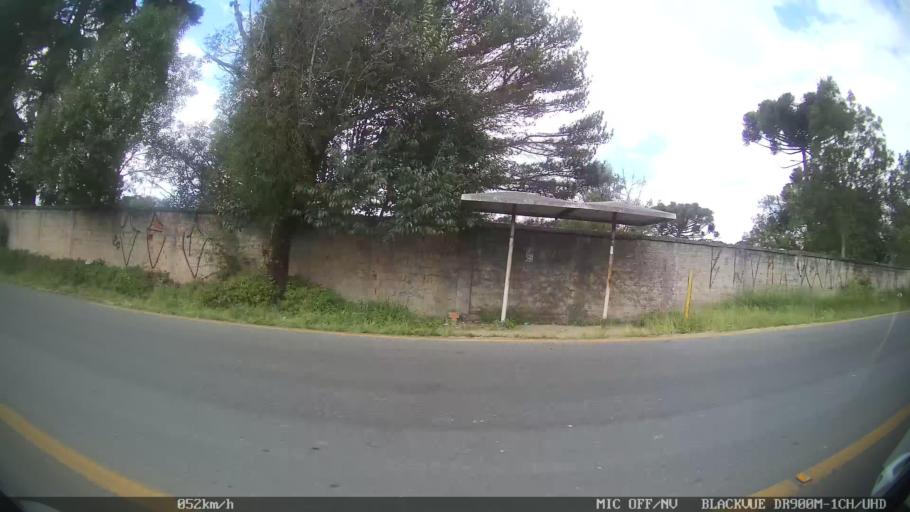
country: BR
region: Parana
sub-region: Pinhais
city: Pinhais
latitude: -25.3710
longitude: -49.2170
